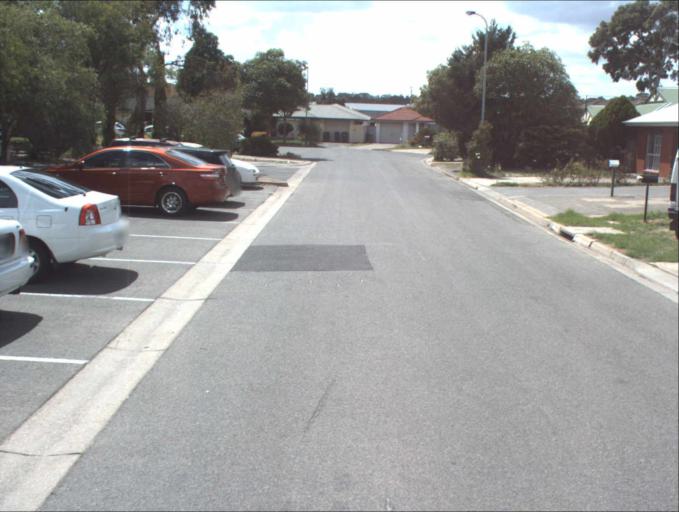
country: AU
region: South Australia
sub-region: Port Adelaide Enfield
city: Enfield
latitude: -34.8494
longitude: 138.5984
